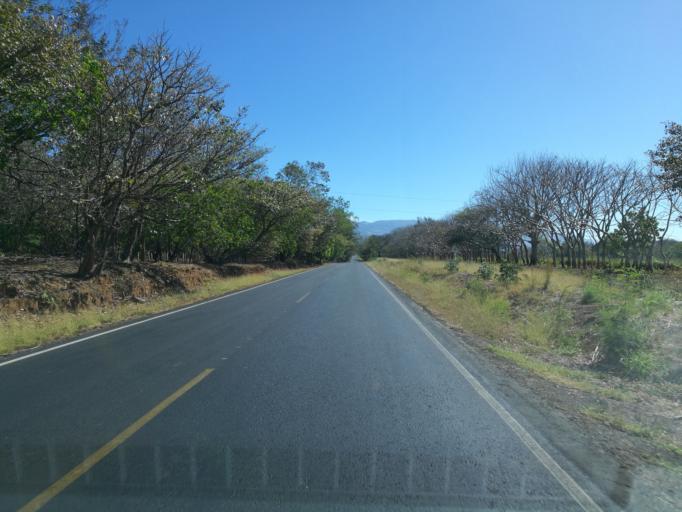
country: CR
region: Puntarenas
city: Miramar
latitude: 10.0899
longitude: -84.8302
